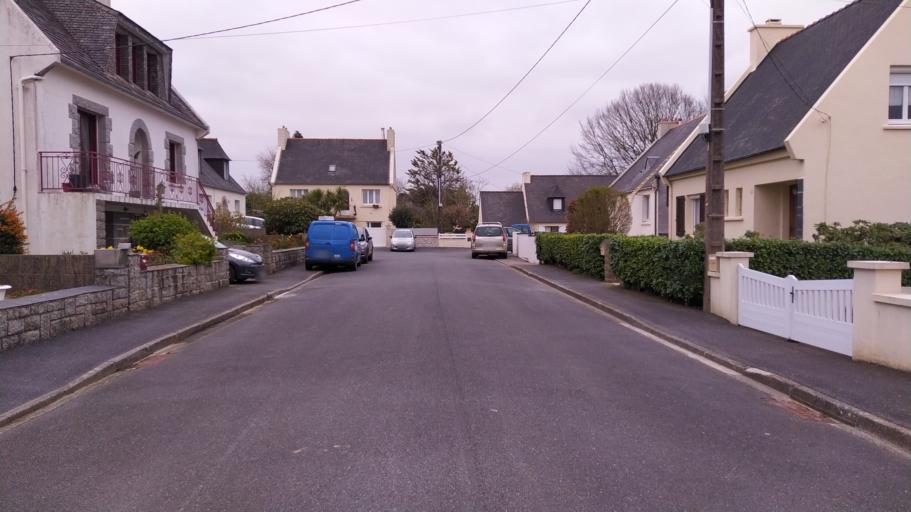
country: FR
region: Brittany
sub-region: Departement du Finistere
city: Landivisiau
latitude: 48.5008
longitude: -4.0735
